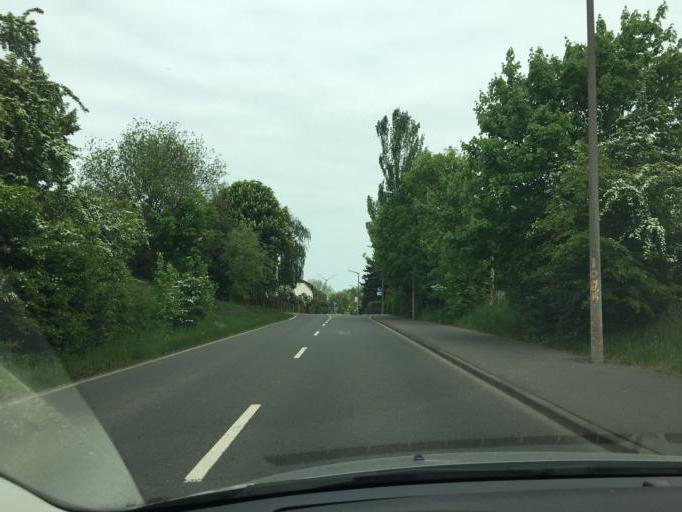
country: DE
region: Saxony
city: Rackwitz
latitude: 51.4018
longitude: 12.4082
